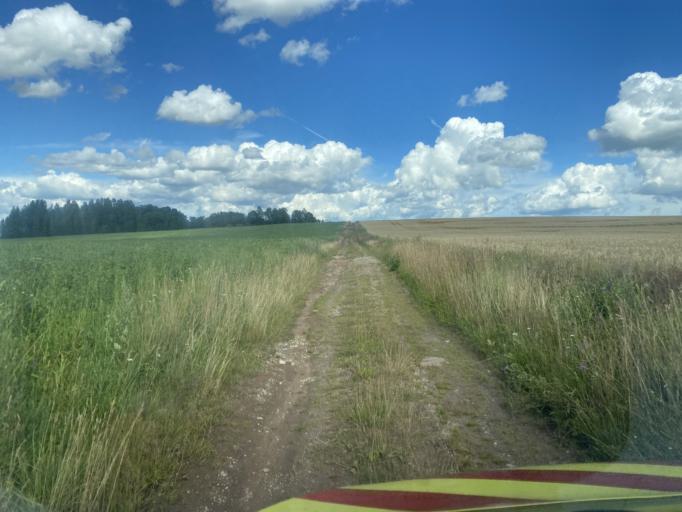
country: EE
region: Viljandimaa
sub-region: Viljandi linn
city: Viljandi
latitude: 58.2913
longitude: 25.6032
